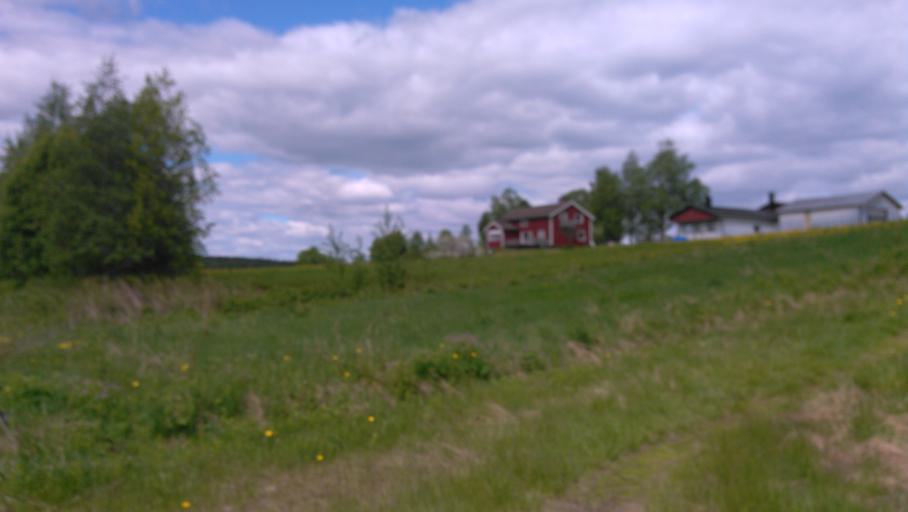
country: SE
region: Vaesterbotten
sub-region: Umea Kommun
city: Roback
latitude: 63.8857
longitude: 20.0369
